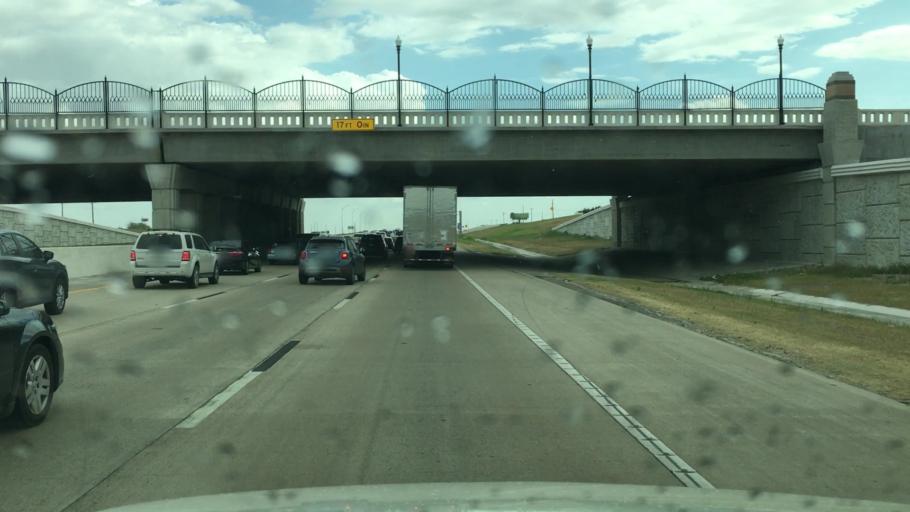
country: US
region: Texas
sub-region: McLennan County
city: Lorena
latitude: 31.3612
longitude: -97.2178
